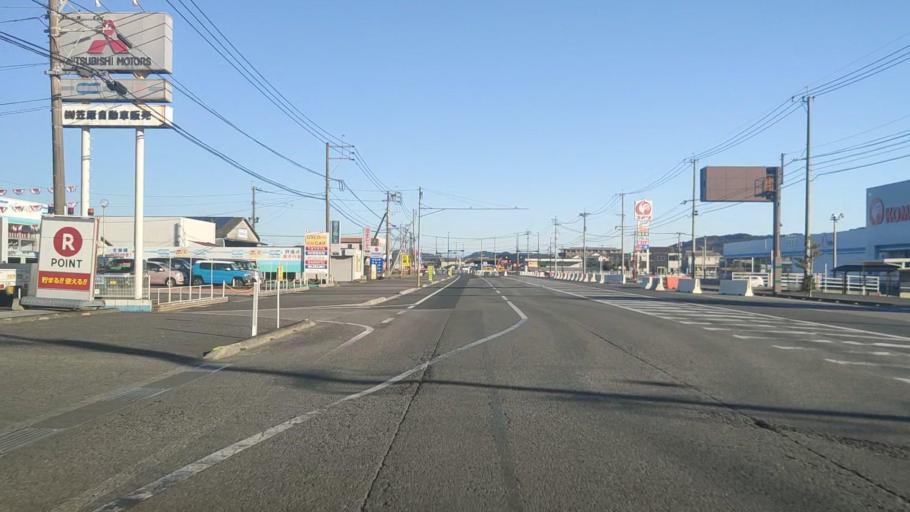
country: JP
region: Miyazaki
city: Nobeoka
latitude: 32.4001
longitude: 131.6303
